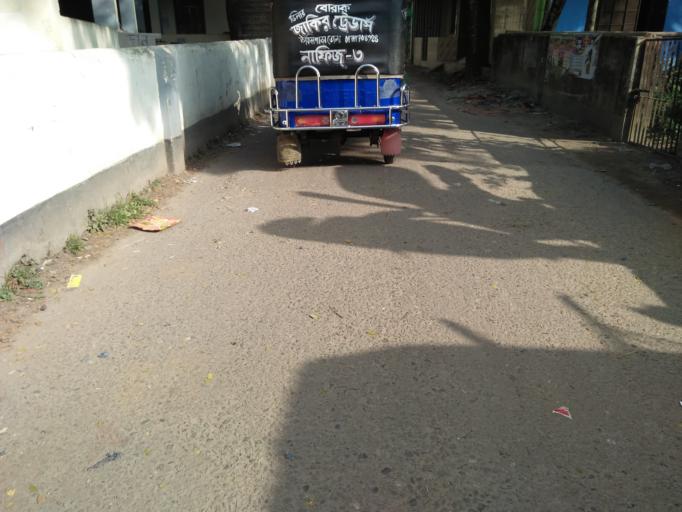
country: BD
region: Barisal
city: Bhola
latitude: 22.6786
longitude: 90.6422
